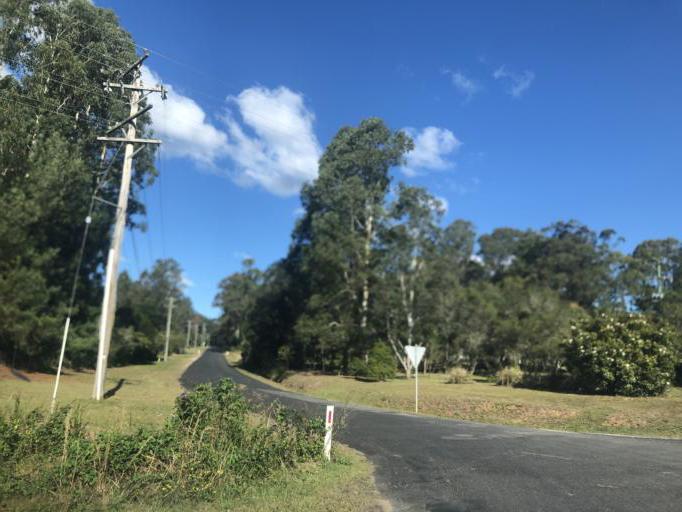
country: AU
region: New South Wales
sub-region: Coffs Harbour
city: Nana Glen
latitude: -30.0530
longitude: 152.9845
